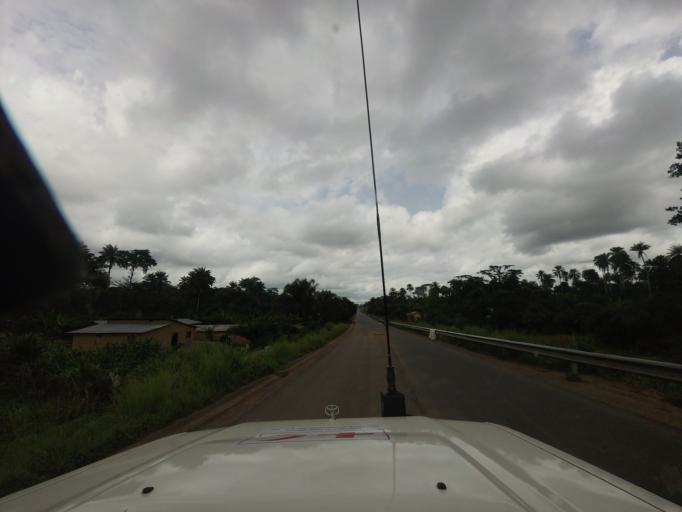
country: GN
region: Nzerekore
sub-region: Macenta
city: Macenta
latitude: 8.2814
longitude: -9.1770
